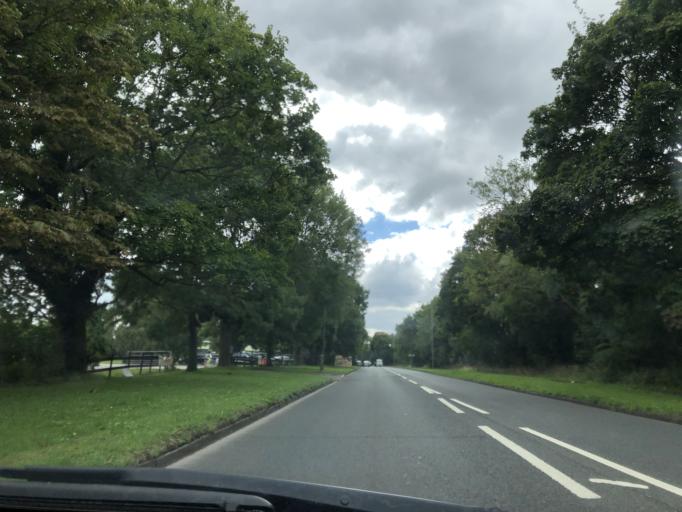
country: GB
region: England
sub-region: Kent
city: Halstead
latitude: 51.3512
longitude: 0.1298
